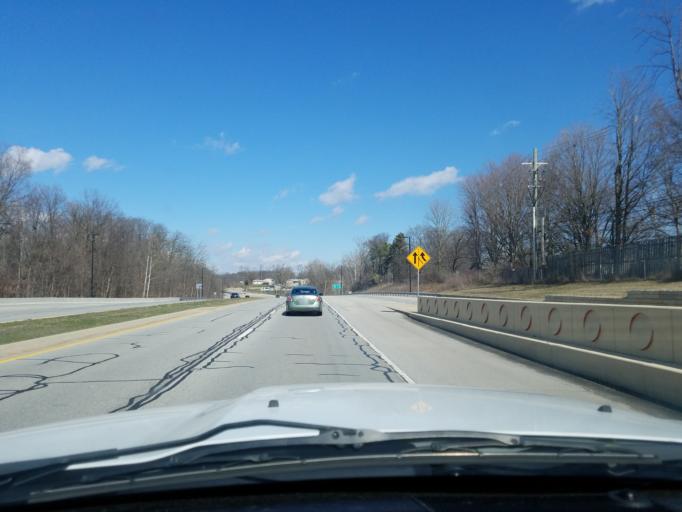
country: US
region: Indiana
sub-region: Hamilton County
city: Carmel
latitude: 39.9801
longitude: -86.1127
